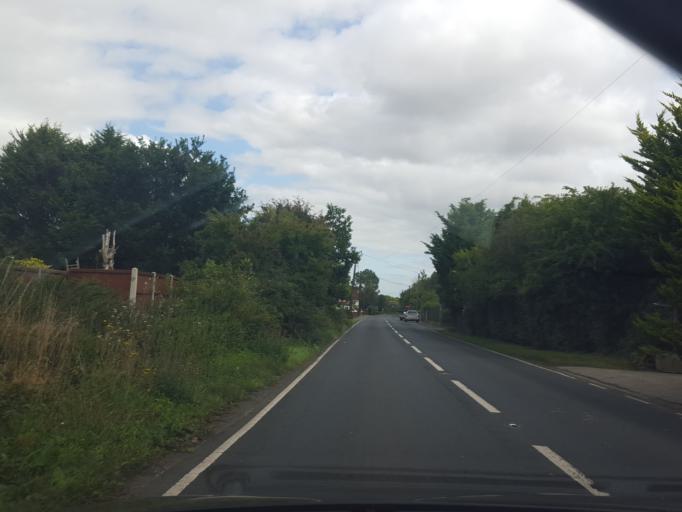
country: GB
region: England
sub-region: Essex
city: Great Bentley
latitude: 51.8822
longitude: 1.0382
